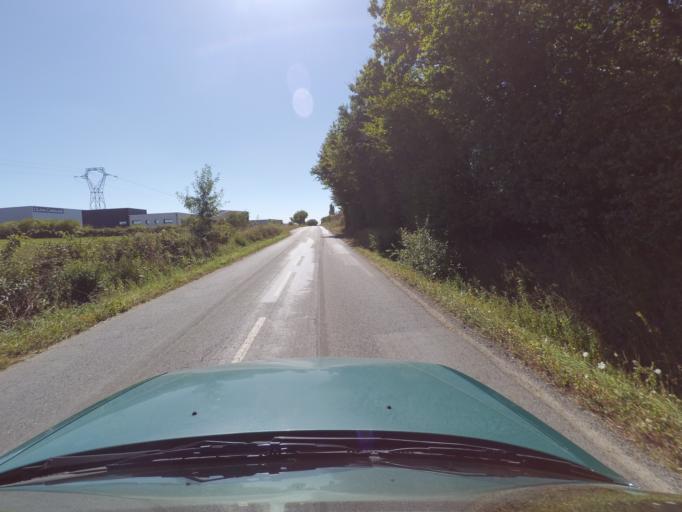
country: FR
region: Pays de la Loire
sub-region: Departement de la Loire-Atlantique
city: Les Sorinieres
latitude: 47.1235
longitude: -1.5098
